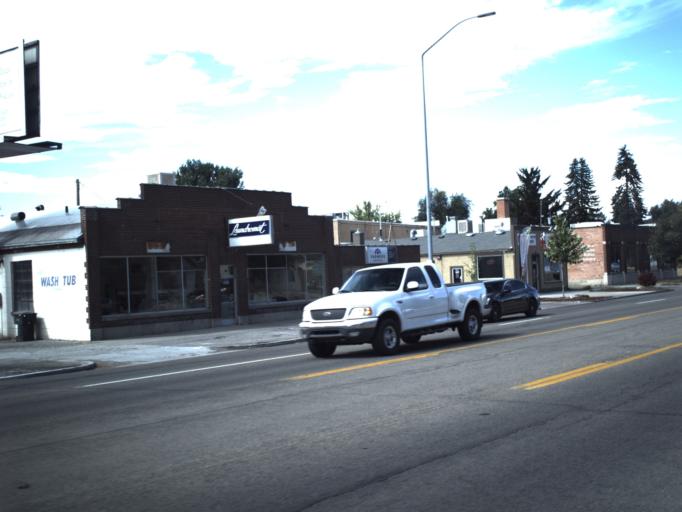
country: US
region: Utah
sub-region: Cache County
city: Logan
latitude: 41.7222
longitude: -111.8352
